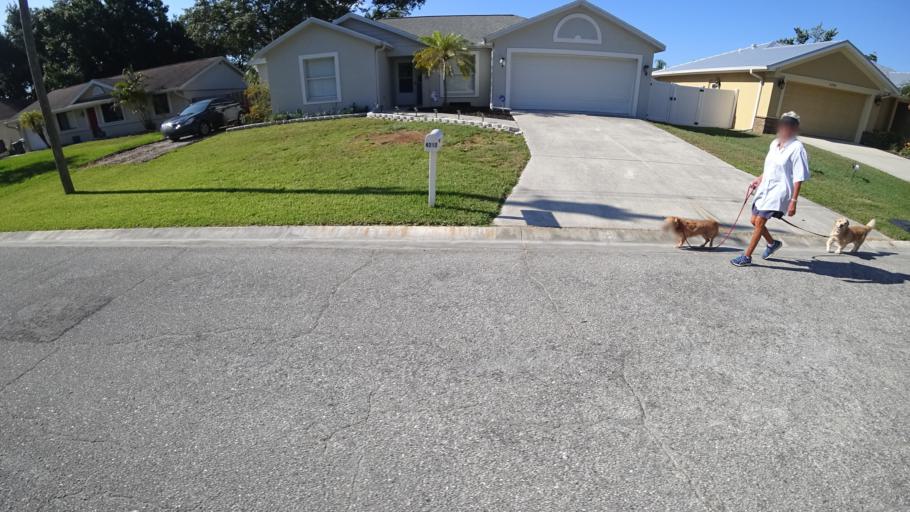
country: US
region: Florida
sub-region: Manatee County
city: Ellenton
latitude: 27.5014
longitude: -82.5108
